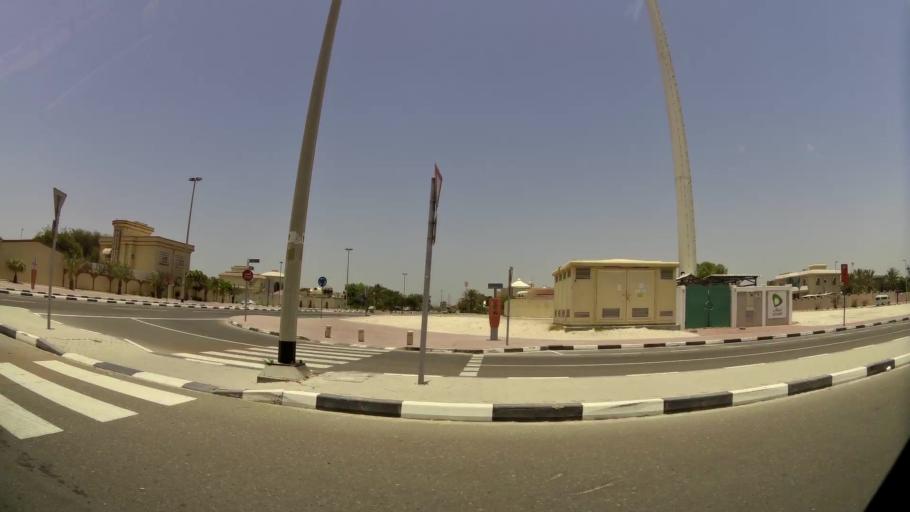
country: AE
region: Ash Shariqah
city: Sharjah
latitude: 25.2354
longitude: 55.2891
